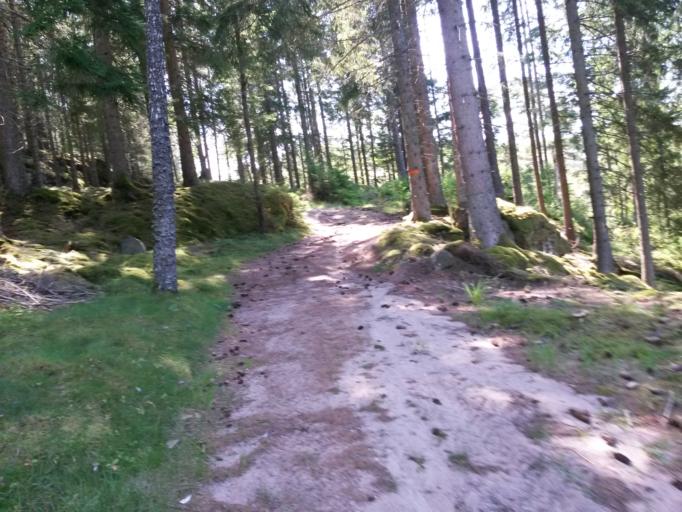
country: SE
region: Vaestra Goetaland
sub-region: Vargarda Kommun
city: Jonstorp
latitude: 57.9686
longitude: 12.6842
